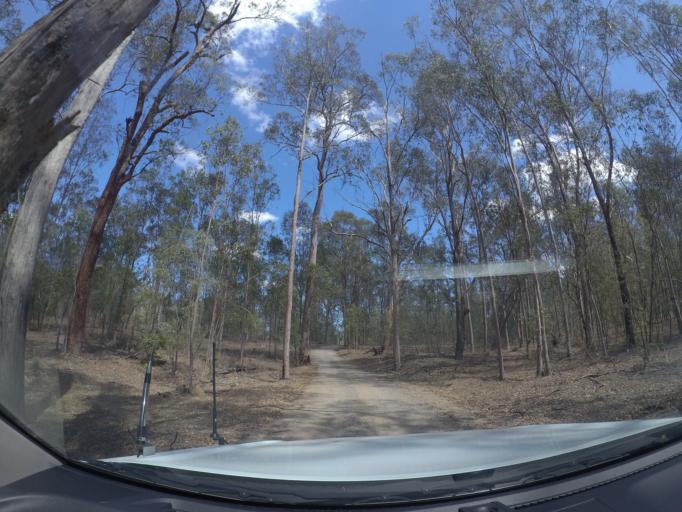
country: AU
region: Queensland
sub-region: Logan
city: North Maclean
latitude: -27.8339
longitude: 152.9421
